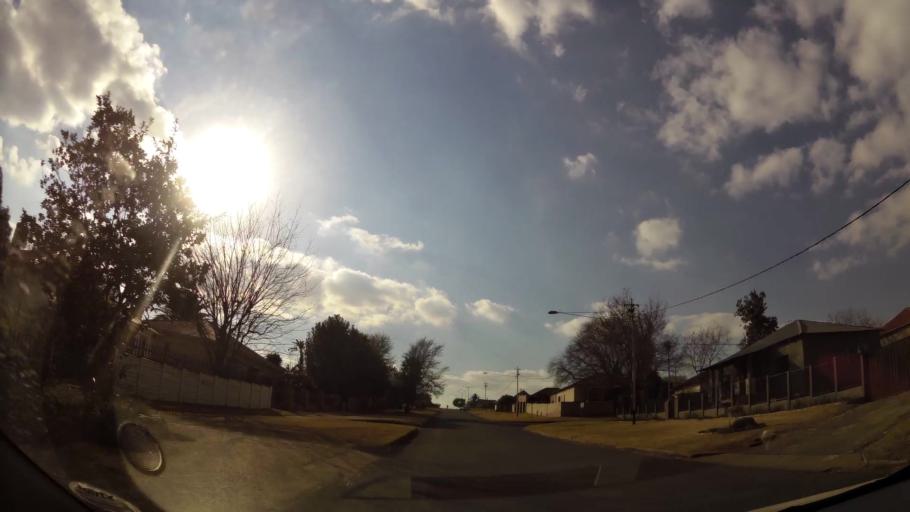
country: ZA
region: Gauteng
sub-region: West Rand District Municipality
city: Krugersdorp
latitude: -26.0860
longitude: 27.7651
